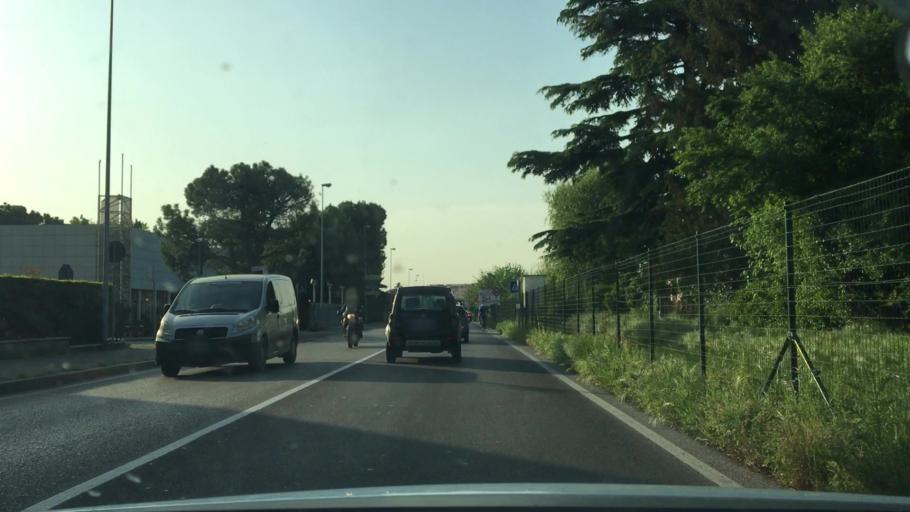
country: IT
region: Veneto
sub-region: Provincia di Verona
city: Verona
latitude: 45.4103
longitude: 11.0032
